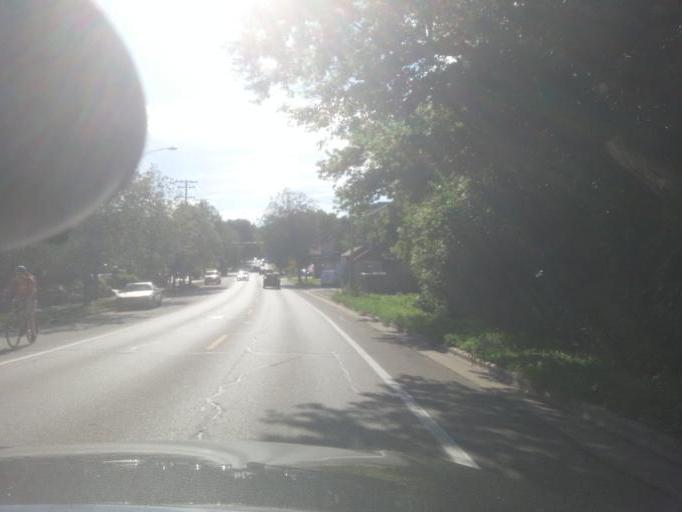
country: US
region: Wisconsin
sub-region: Dane County
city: Shorewood Hills
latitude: 43.0743
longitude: -89.4714
